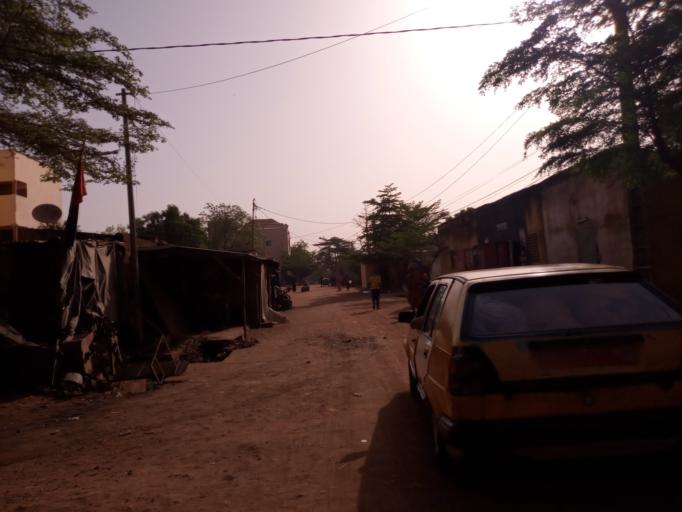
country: ML
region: Bamako
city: Bamako
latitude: 12.6568
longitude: -7.9882
